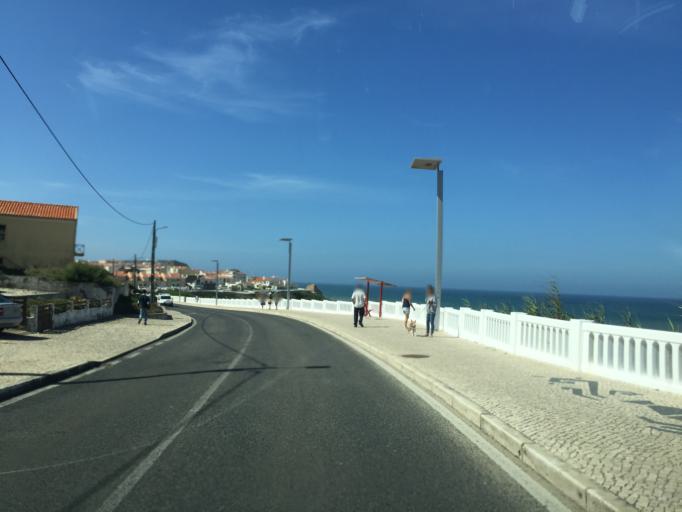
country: PT
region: Lisbon
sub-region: Torres Vedras
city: Silveira
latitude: 39.1388
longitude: -9.3786
